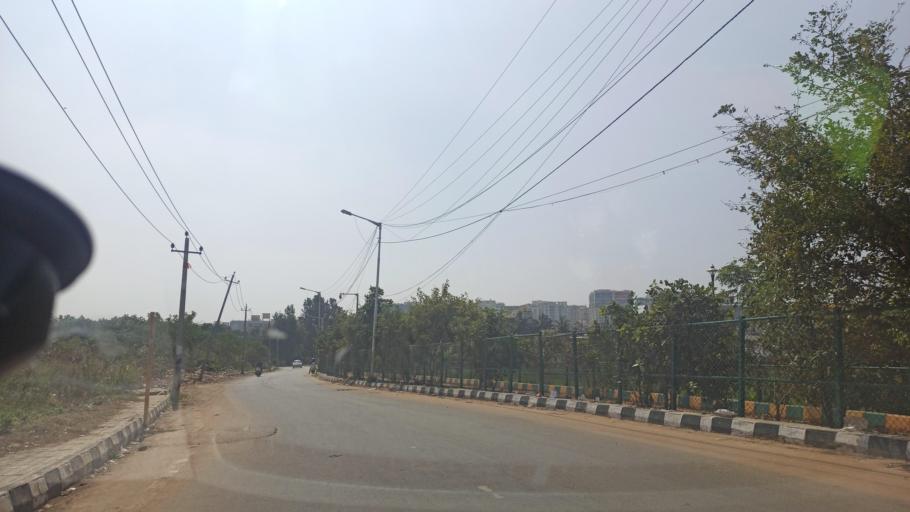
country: IN
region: Karnataka
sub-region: Bangalore Urban
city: Yelahanka
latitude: 13.0622
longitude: 77.5998
